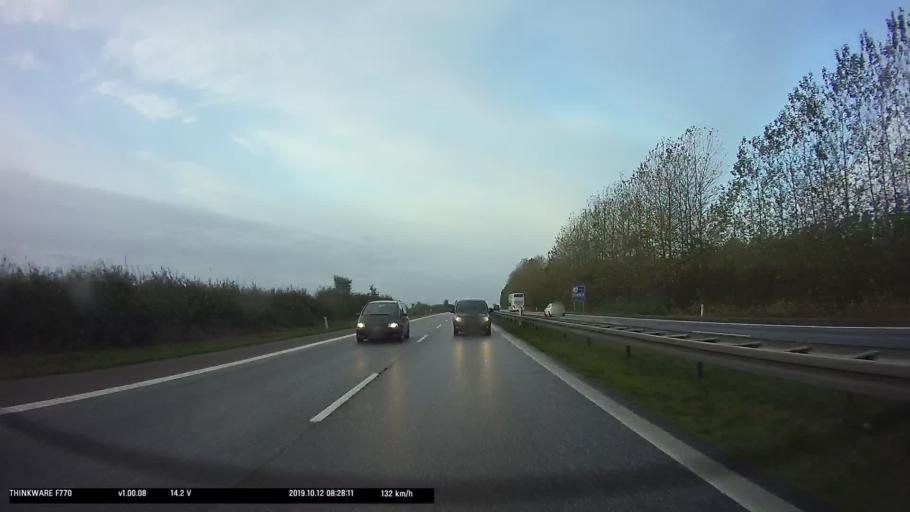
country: DK
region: Central Jutland
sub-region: Hedensted Kommune
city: Hedensted
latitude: 55.8353
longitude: 9.7222
